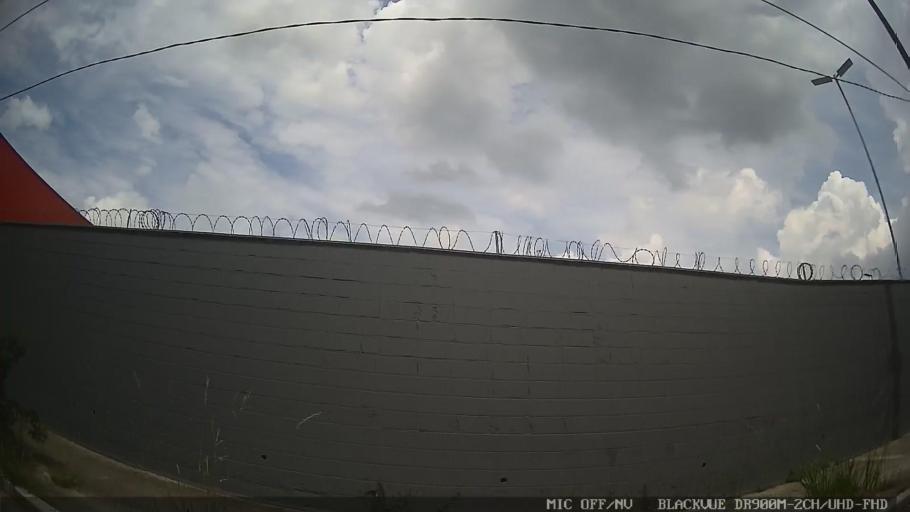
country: BR
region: Sao Paulo
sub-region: Ribeirao Pires
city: Ribeirao Pires
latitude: -23.7056
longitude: -46.3993
